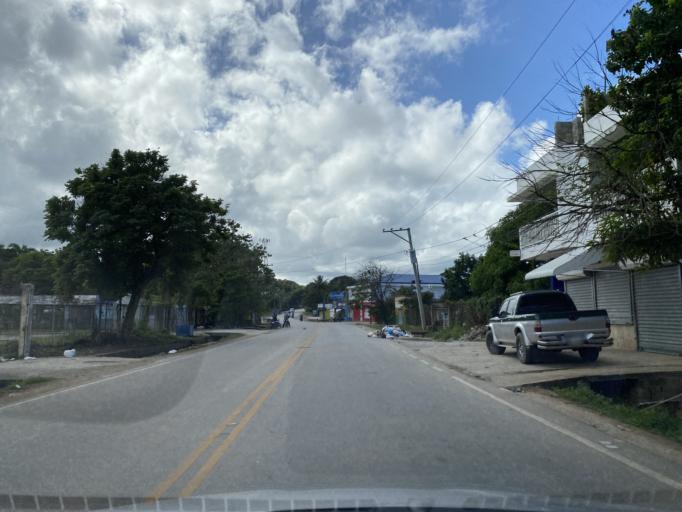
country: DO
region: Samana
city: Las Terrenas
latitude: 19.3073
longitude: -69.5387
